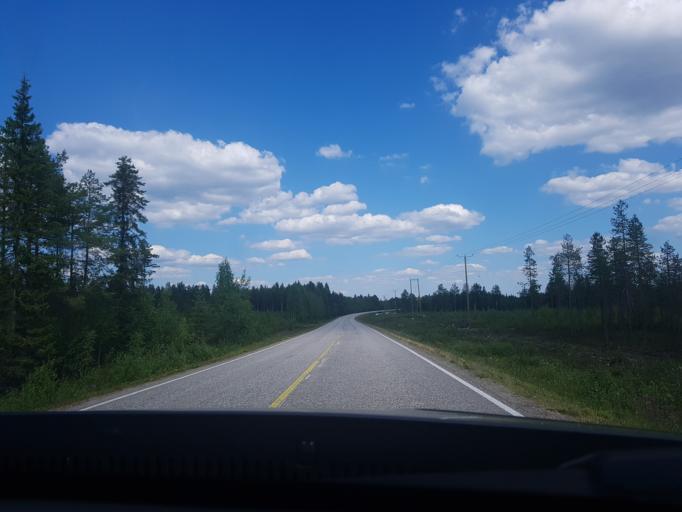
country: FI
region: Kainuu
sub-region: Kehys-Kainuu
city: Kuhmo
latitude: 64.2110
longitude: 29.7573
